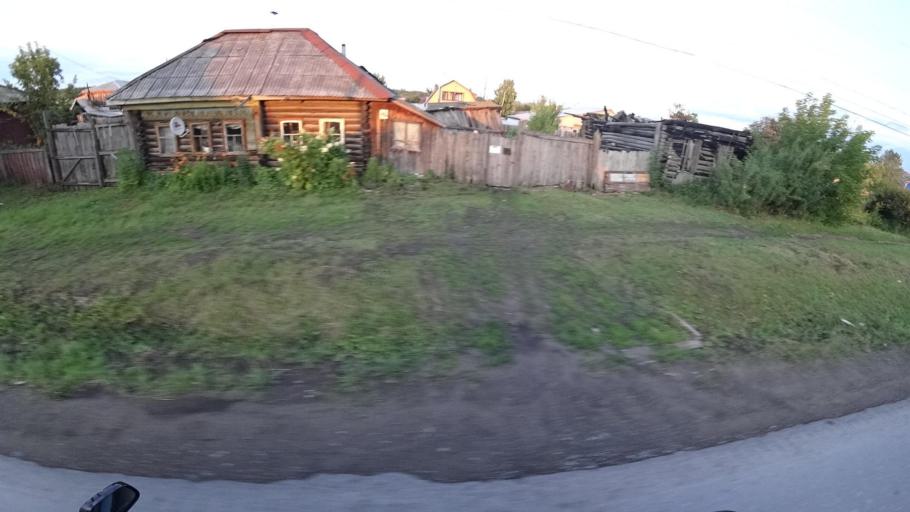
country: RU
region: Sverdlovsk
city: Kamyshlov
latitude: 56.8630
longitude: 62.7093
